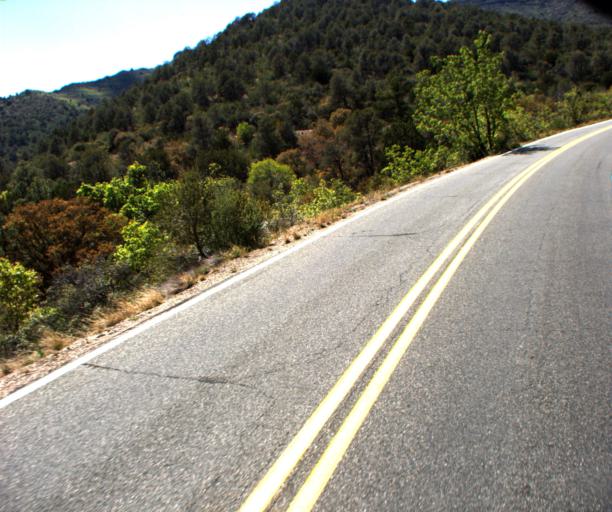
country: US
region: Arizona
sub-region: Yavapai County
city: Clarkdale
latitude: 34.7414
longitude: -112.1382
